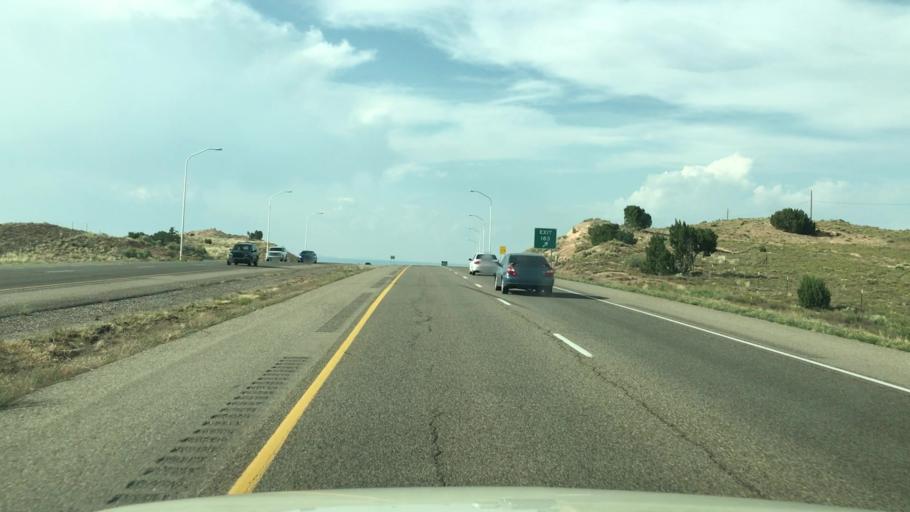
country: US
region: New Mexico
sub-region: Santa Fe County
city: Pojoaque
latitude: 35.9226
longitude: -106.0169
